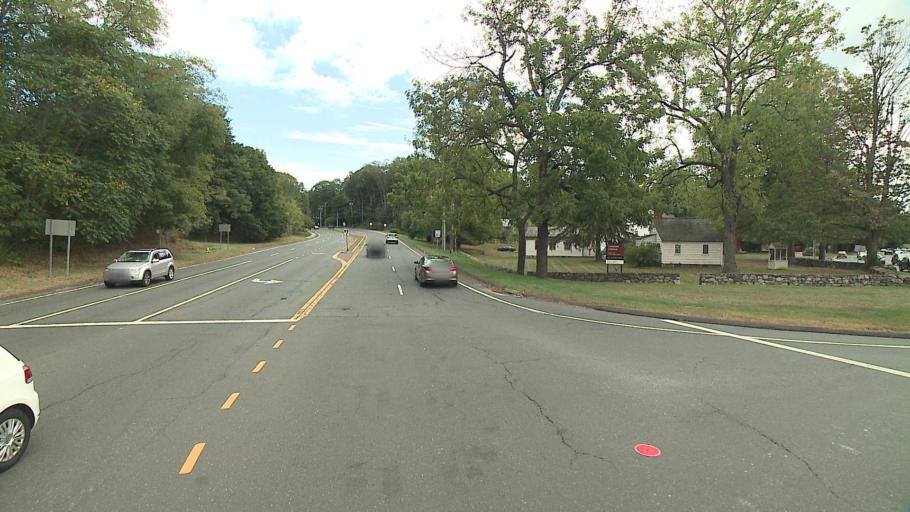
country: US
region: Connecticut
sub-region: Fairfield County
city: Wilton
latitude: 41.1815
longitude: -73.4160
